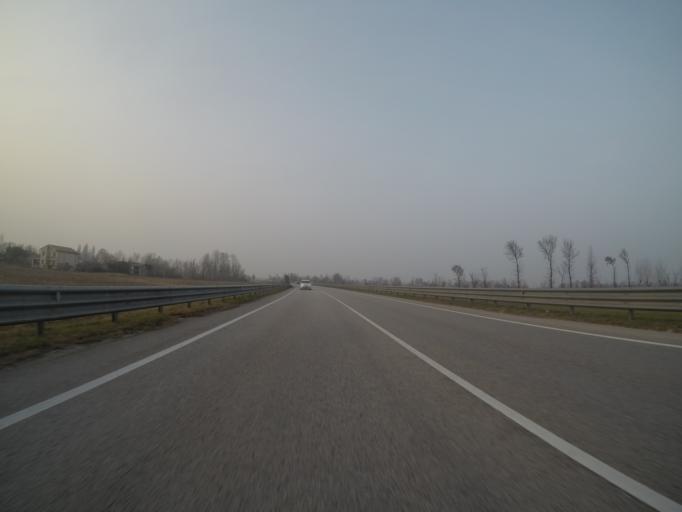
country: IT
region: Veneto
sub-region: Provincia di Treviso
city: Resana
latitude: 45.6335
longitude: 11.9348
